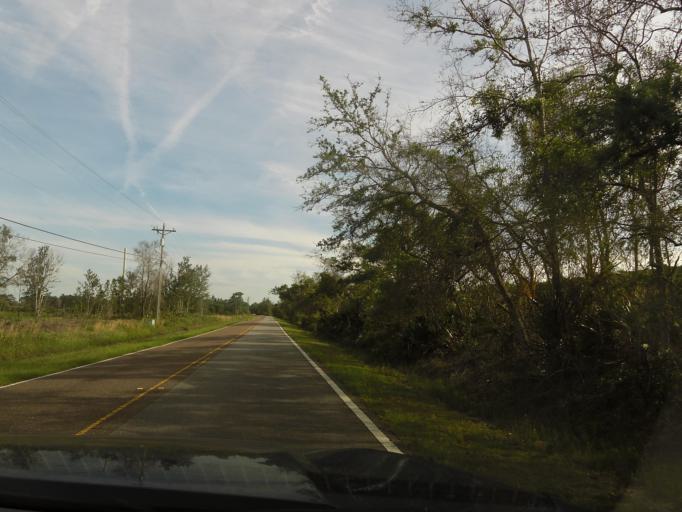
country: US
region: Florida
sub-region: Nassau County
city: Fernandina Beach
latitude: 30.4979
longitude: -81.4721
